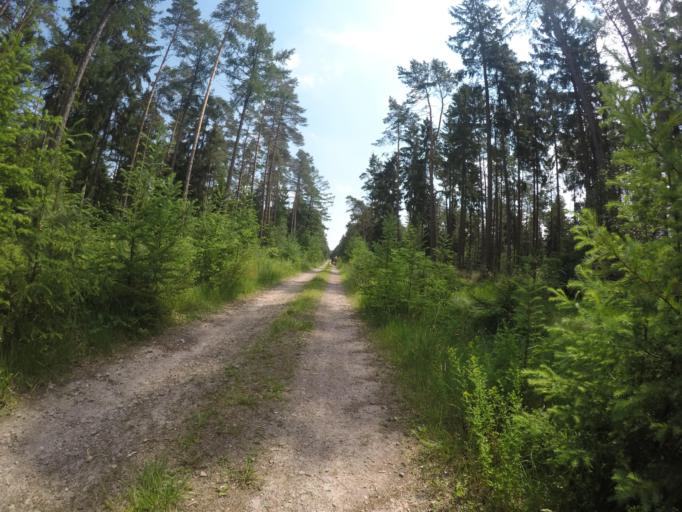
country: DE
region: Lower Saxony
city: Asendorf
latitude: 53.2557
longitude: 9.9396
